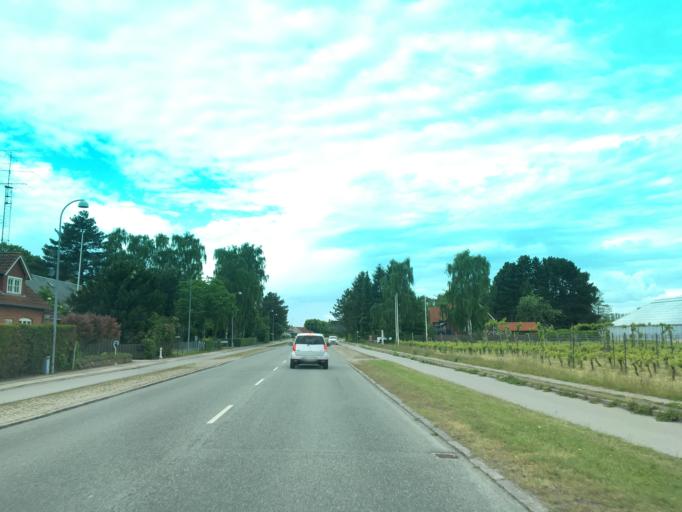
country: DK
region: Capital Region
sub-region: Hvidovre Kommune
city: Hvidovre
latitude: 55.6395
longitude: 12.4474
